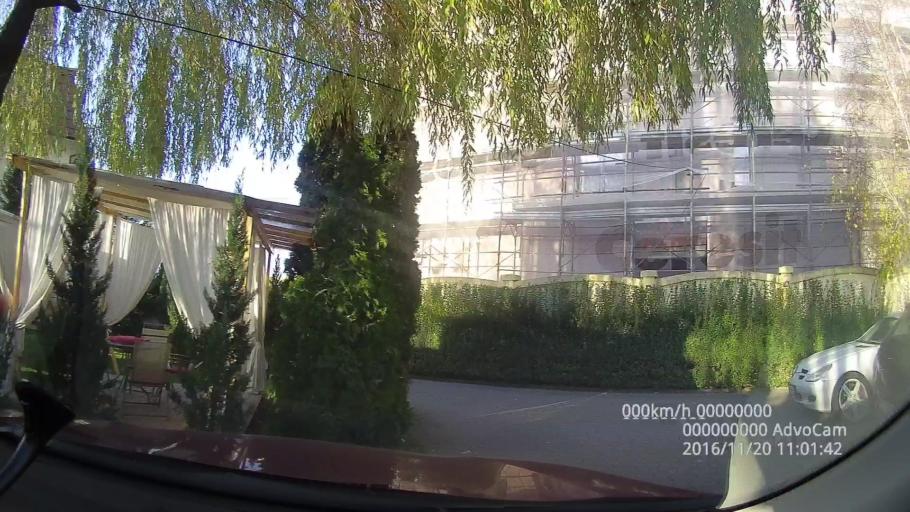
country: RO
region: Timis
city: Timisoara
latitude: 45.7729
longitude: 21.2362
